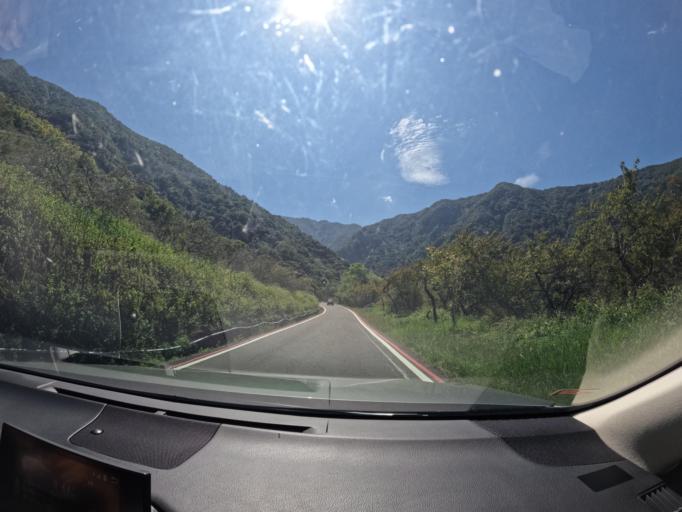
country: TW
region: Taiwan
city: Yujing
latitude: 23.2638
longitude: 120.8500
